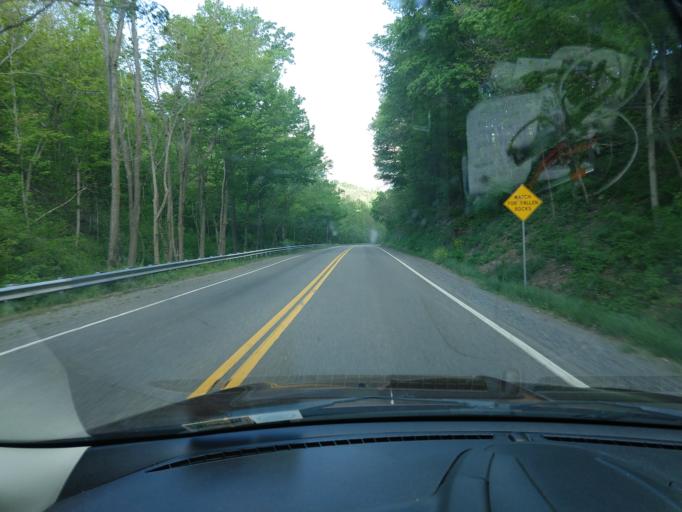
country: US
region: Virginia
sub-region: Russell County
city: Honaker
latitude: 36.9686
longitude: -81.9398
